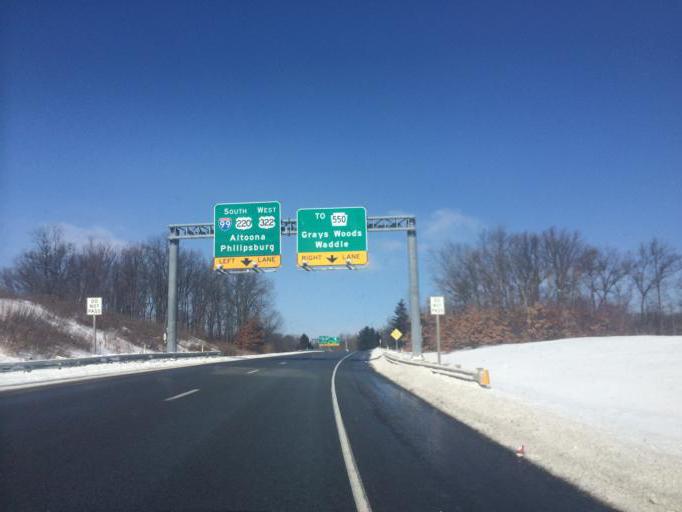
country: US
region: Pennsylvania
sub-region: Centre County
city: Park Forest Village
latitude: 40.8141
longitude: -77.9257
